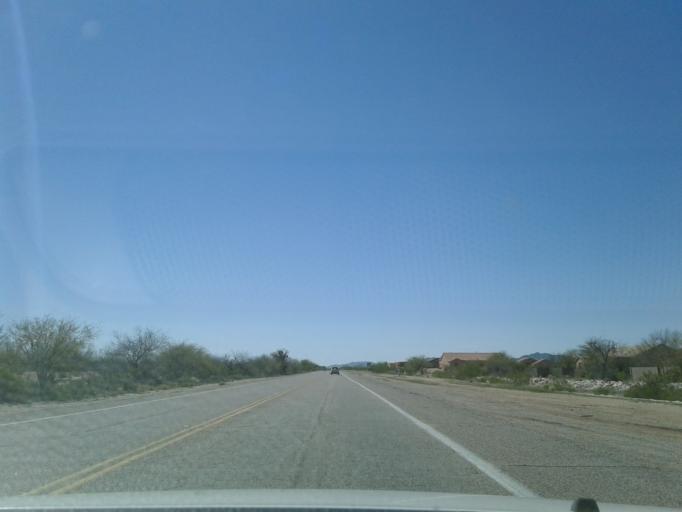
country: US
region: Arizona
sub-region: Pima County
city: Avra Valley
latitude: 32.3892
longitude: -111.3067
